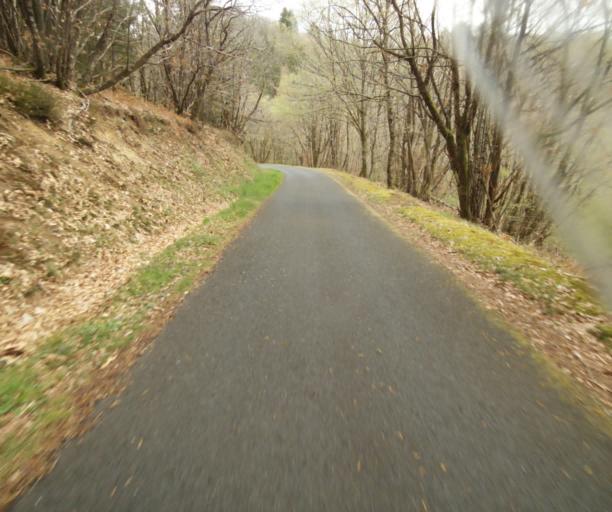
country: FR
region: Limousin
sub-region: Departement de la Correze
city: Naves
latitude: 45.3033
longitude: 1.8104
